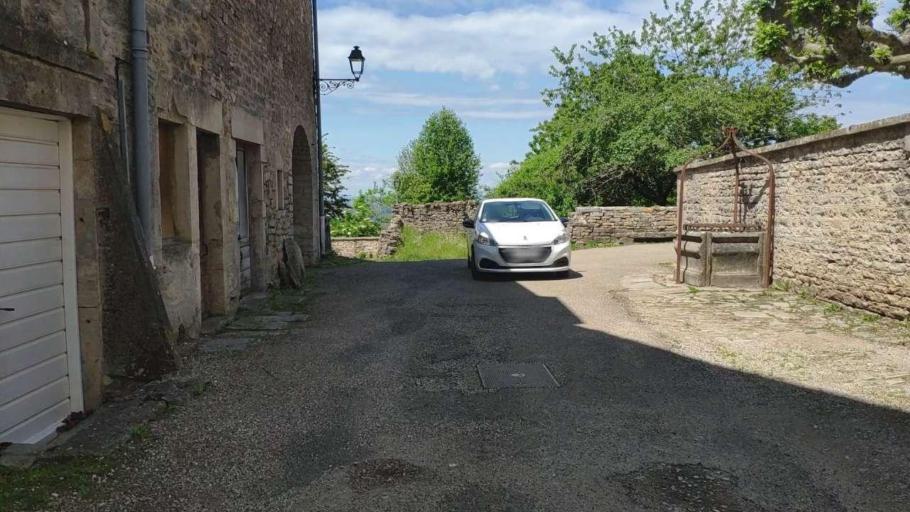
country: FR
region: Franche-Comte
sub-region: Departement du Jura
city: Perrigny
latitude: 46.7535
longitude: 5.6246
